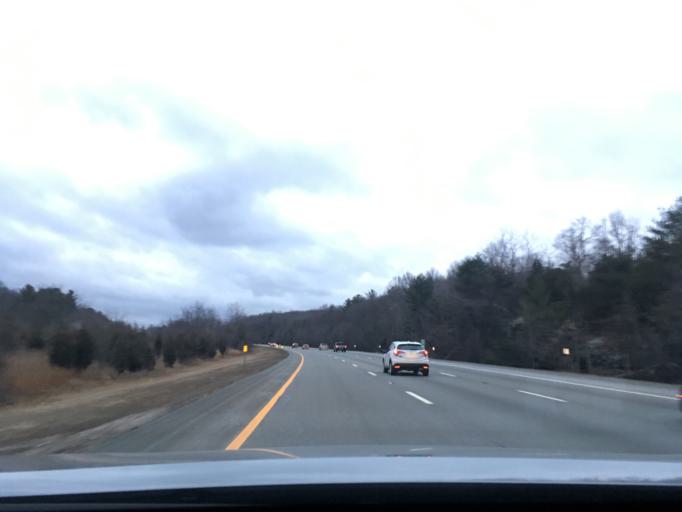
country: US
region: Rhode Island
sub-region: Providence County
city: Smithfield
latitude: 41.8959
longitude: -71.5235
